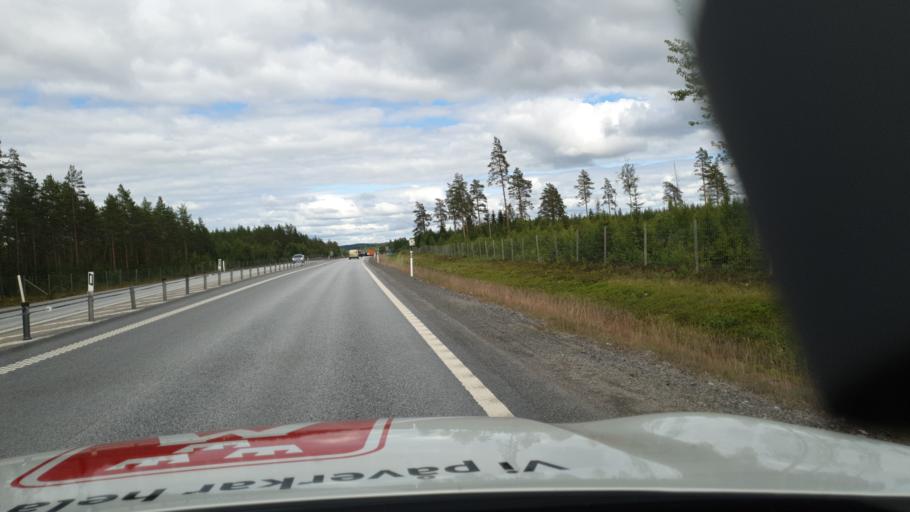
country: SE
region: Vaesterbotten
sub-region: Umea Kommun
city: Hoernefors
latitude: 63.6723
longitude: 19.9810
